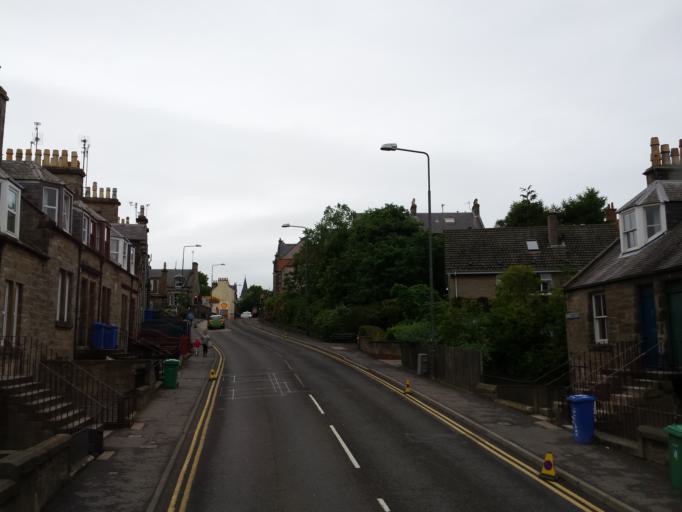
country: GB
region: Scotland
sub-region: Fife
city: Saint Andrews
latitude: 56.3371
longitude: -2.8006
